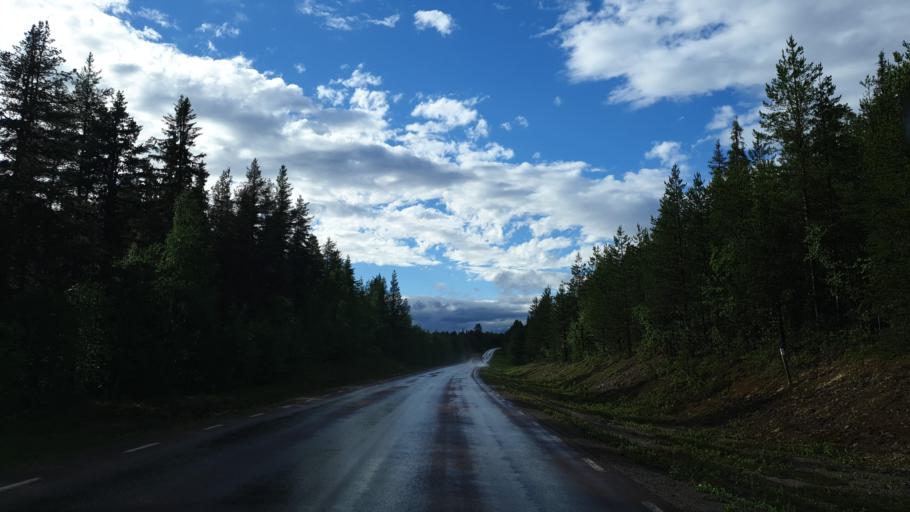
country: SE
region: Norrbotten
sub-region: Arjeplogs Kommun
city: Arjeplog
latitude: 66.0142
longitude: 18.0840
